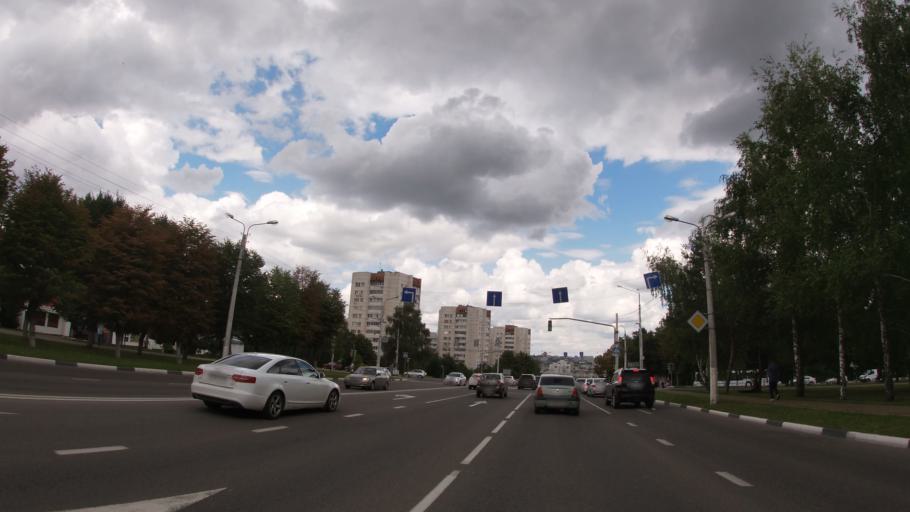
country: RU
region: Belgorod
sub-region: Belgorodskiy Rayon
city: Belgorod
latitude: 50.5780
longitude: 36.5828
